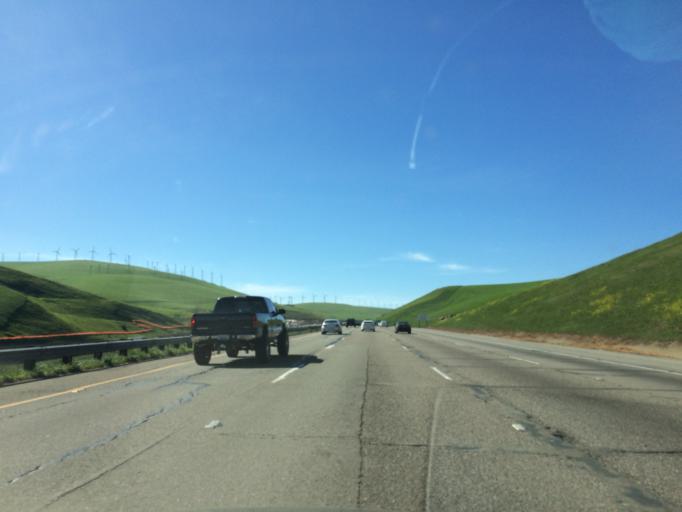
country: US
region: California
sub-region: San Joaquin County
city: Mountain House
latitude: 37.7243
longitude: -121.6495
